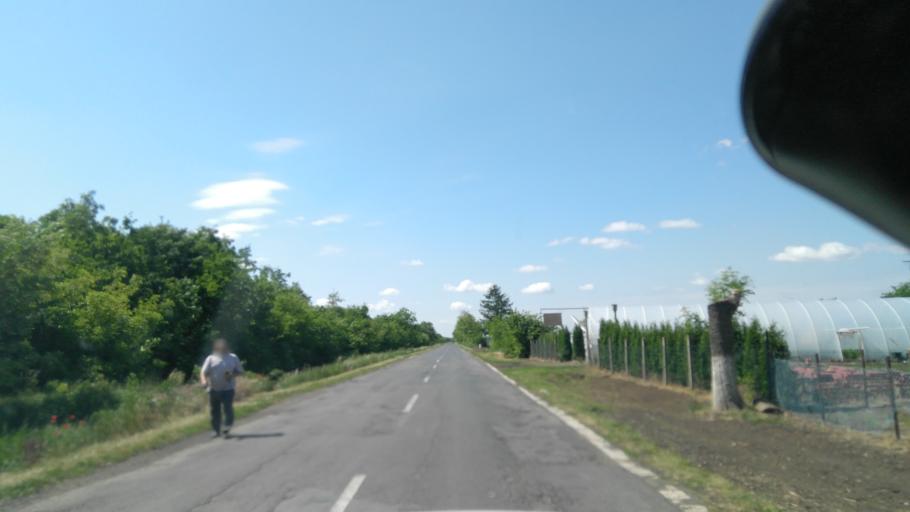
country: HU
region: Bekes
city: Medgyesegyhaza
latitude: 46.4835
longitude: 21.0233
